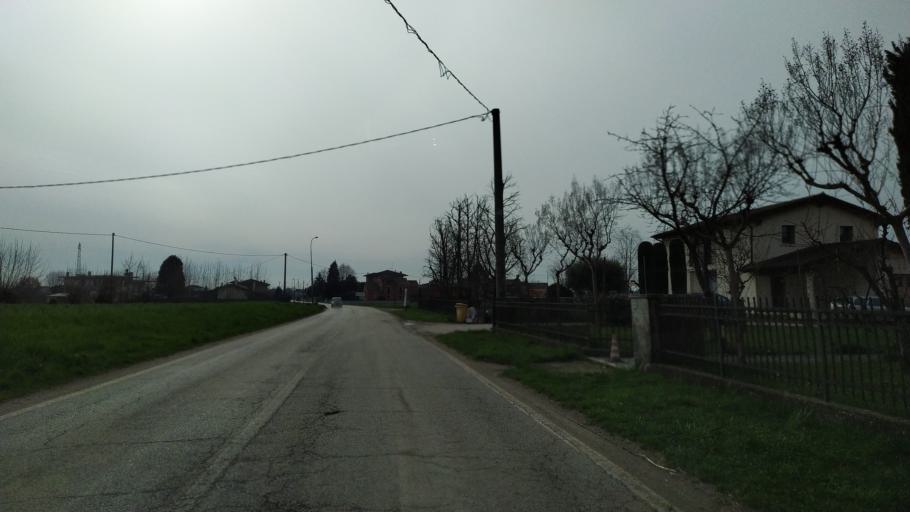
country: IT
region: Veneto
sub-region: Provincia di Padova
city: San Pietro in Gu
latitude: 45.6272
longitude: 11.6692
